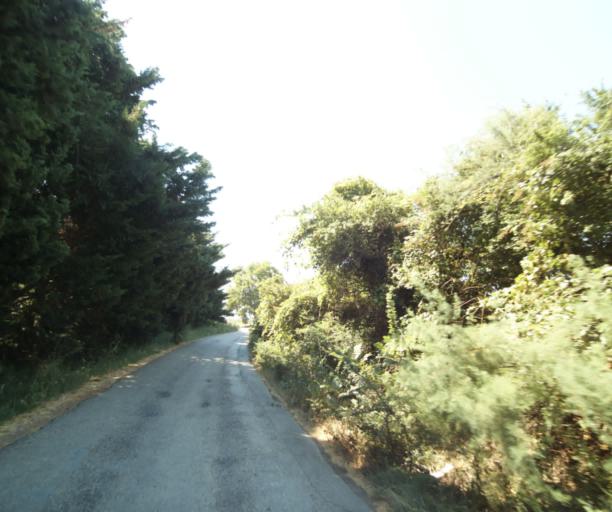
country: FR
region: Languedoc-Roussillon
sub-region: Departement de l'Herault
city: Marsillargues
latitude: 43.6522
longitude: 4.1660
